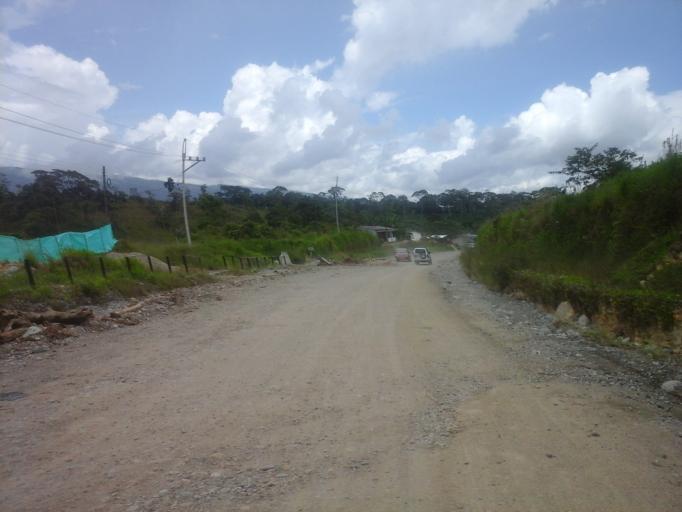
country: CO
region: Putumayo
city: Mocoa
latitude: 1.1758
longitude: -76.6549
